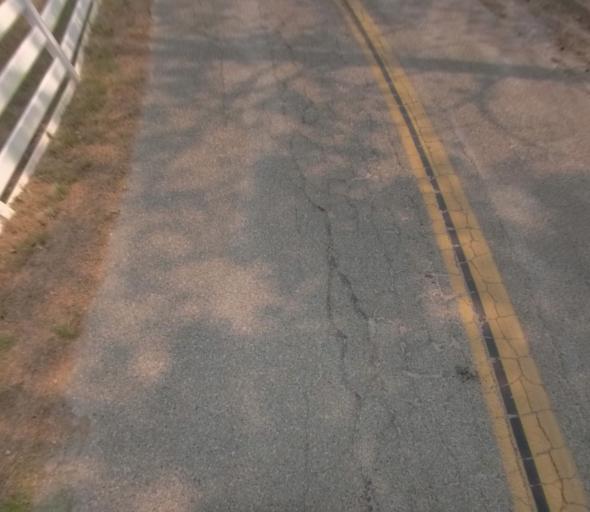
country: US
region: California
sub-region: Madera County
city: Oakhurst
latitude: 37.2997
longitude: -119.6193
